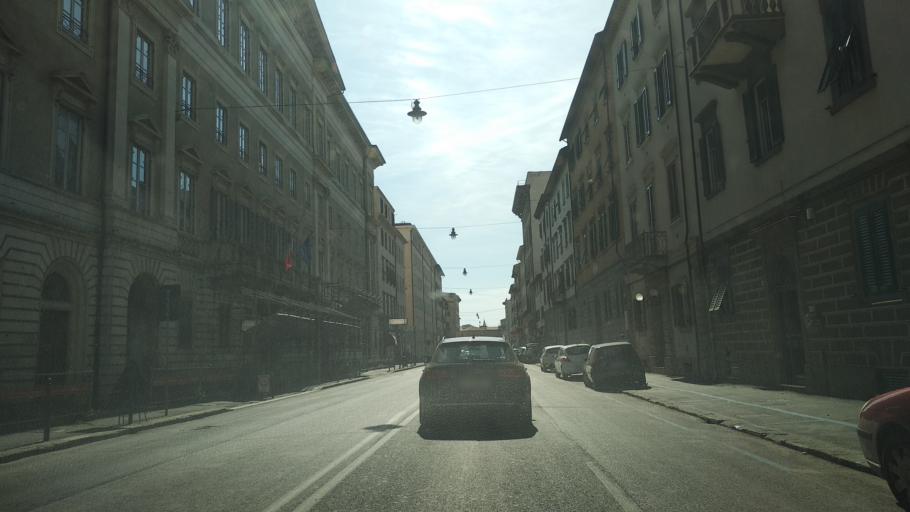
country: IT
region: Tuscany
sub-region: Provincia di Livorno
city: Livorno
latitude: 43.5528
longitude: 10.3184
